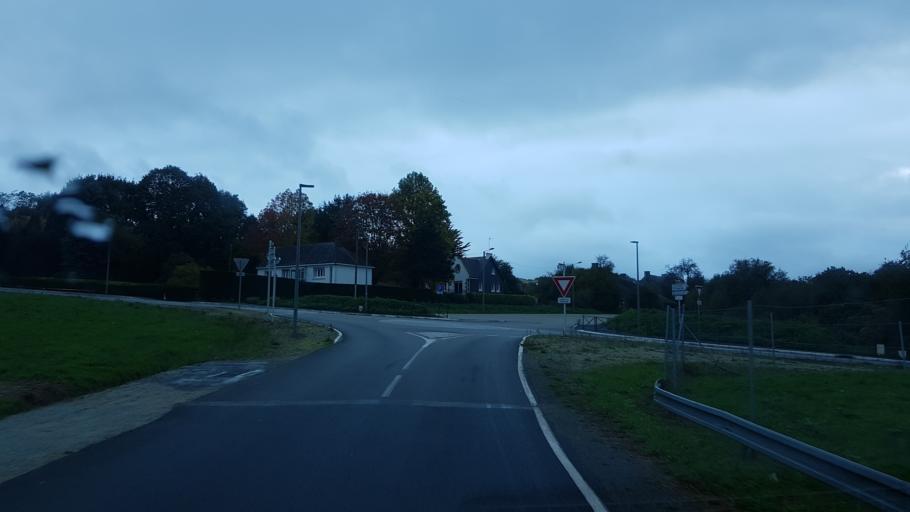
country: FR
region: Brittany
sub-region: Departement du Morbihan
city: Elven
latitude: 47.7254
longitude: -2.5873
